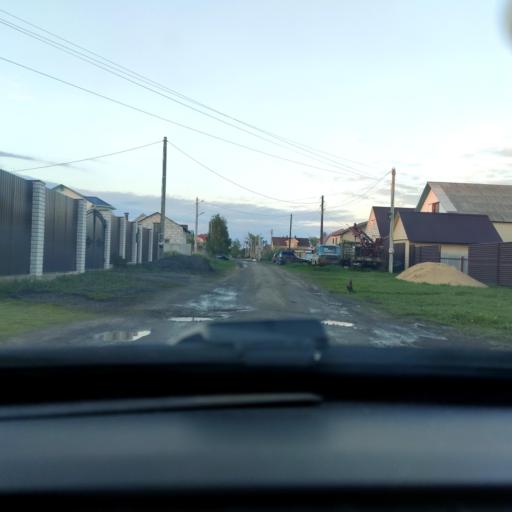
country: RU
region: Voronezj
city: Novaya Usman'
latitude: 51.6537
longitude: 39.4151
